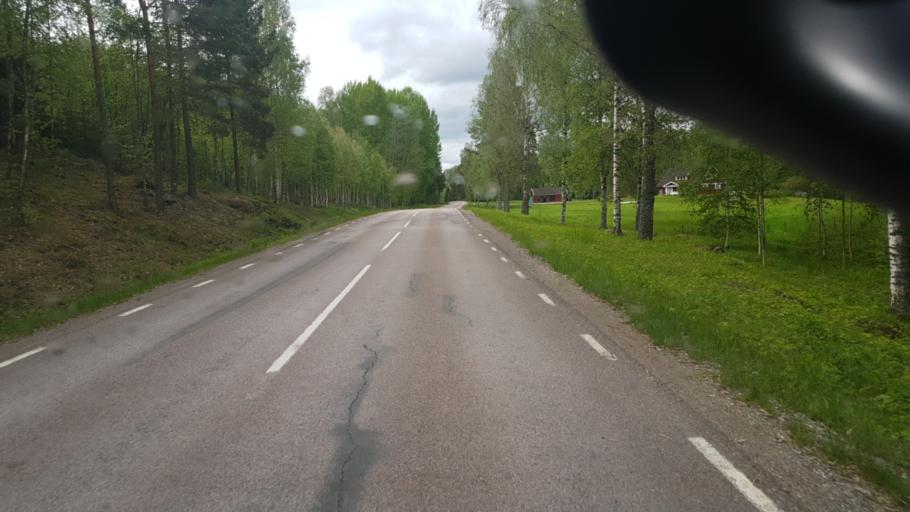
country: SE
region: Vaermland
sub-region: Eda Kommun
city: Amotfors
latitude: 59.8681
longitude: 12.5482
